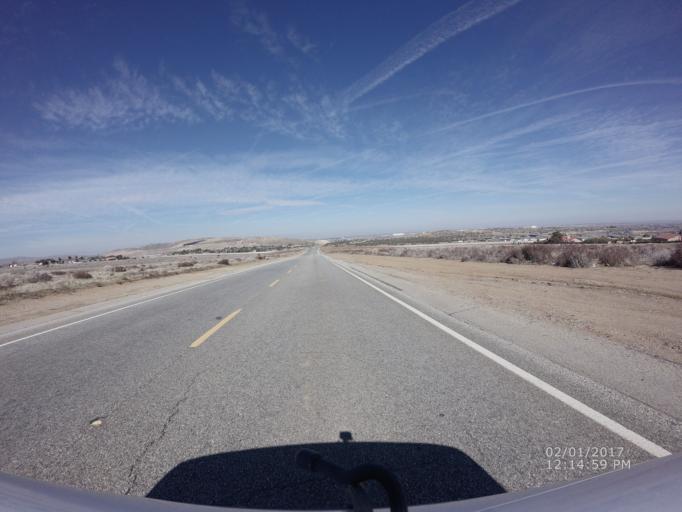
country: US
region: California
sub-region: Los Angeles County
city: Palmdale
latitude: 34.5500
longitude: -118.1413
